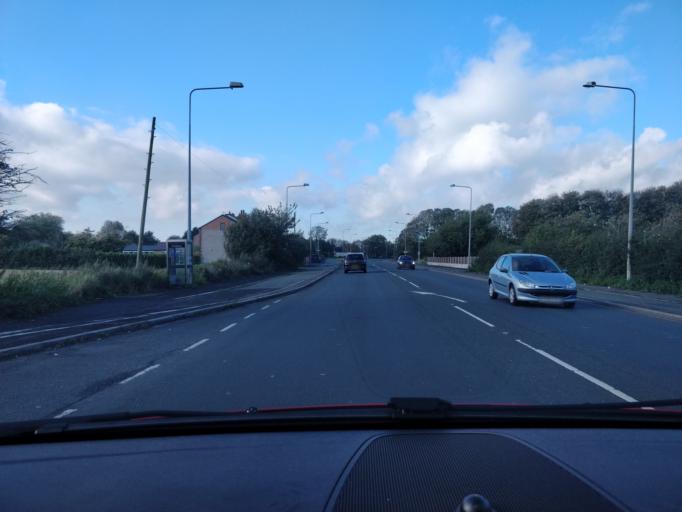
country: GB
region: England
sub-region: Sefton
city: Southport
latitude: 53.6225
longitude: -2.9586
